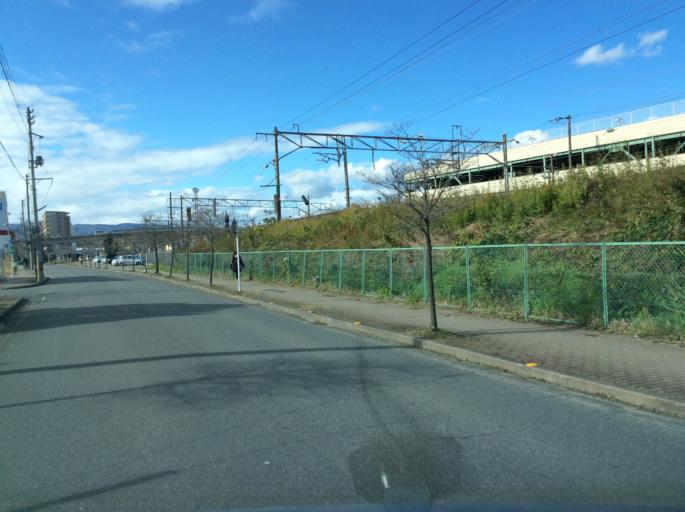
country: JP
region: Fukushima
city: Iwaki
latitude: 37.0581
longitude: 140.9023
